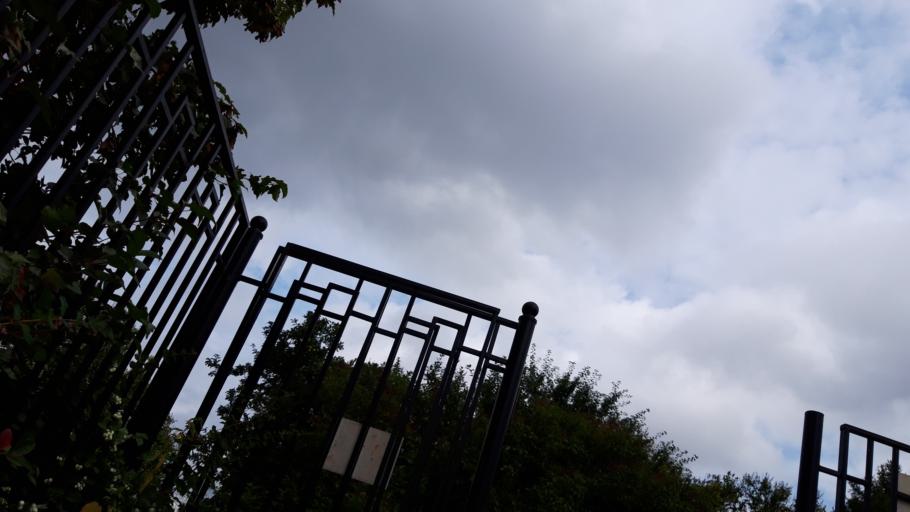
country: RU
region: Moscow
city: Zelenograd
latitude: 55.9844
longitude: 37.2103
